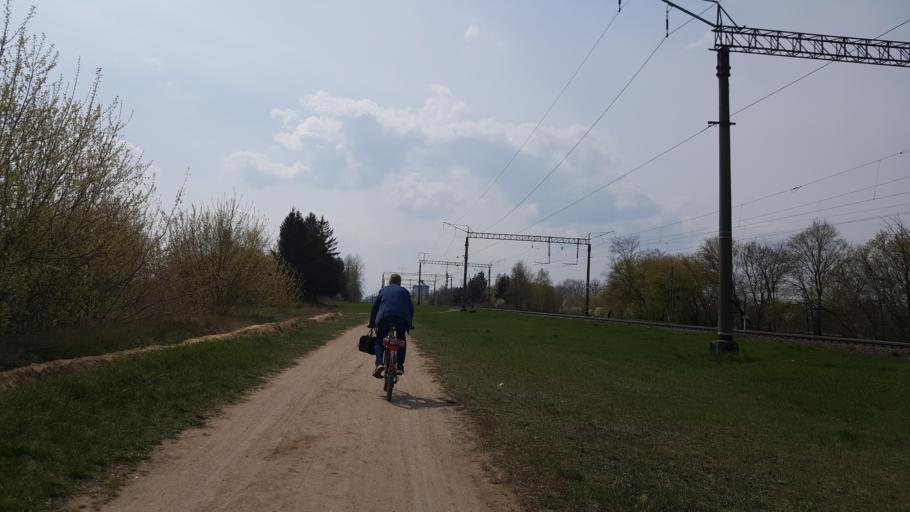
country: BY
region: Brest
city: Zhabinka
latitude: 52.1928
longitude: 23.9967
